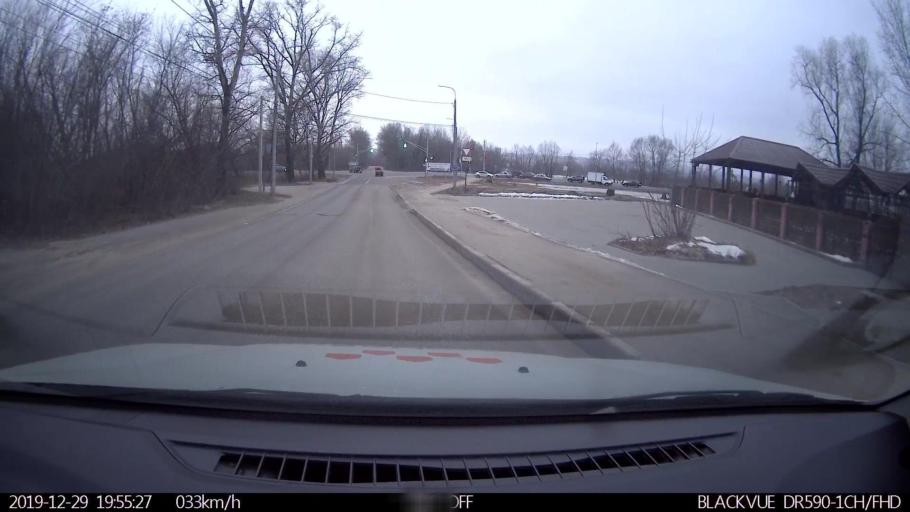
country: RU
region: Nizjnij Novgorod
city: Bor
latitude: 56.3571
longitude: 44.0518
